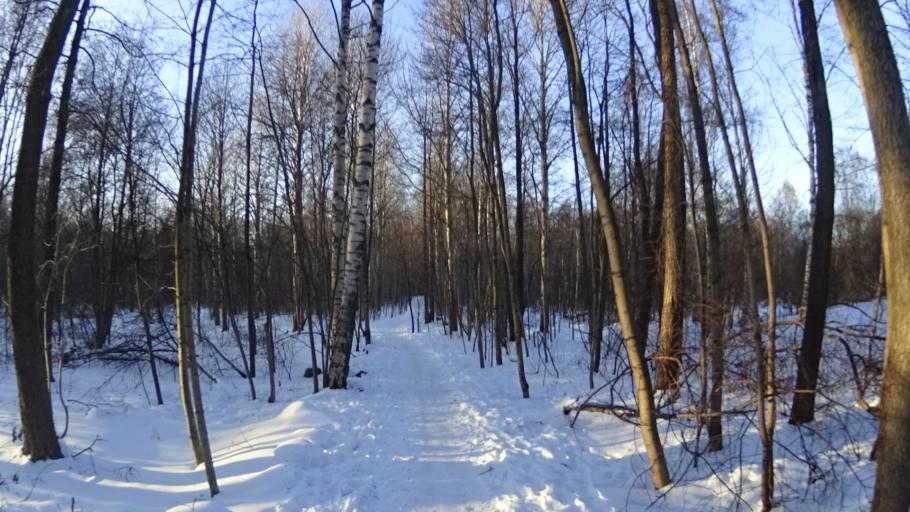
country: FI
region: Uusimaa
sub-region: Helsinki
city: Teekkarikylae
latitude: 60.2110
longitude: 24.8531
